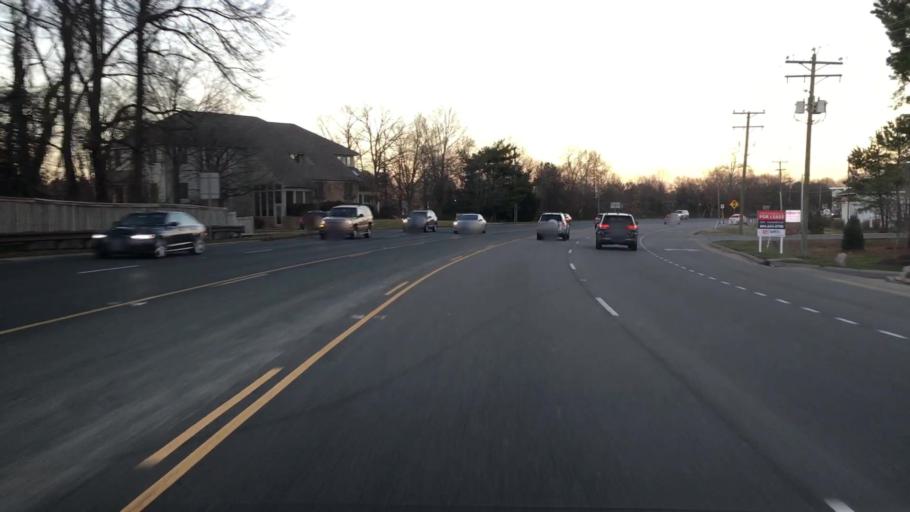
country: US
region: Virginia
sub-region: Chesterfield County
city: Bon Air
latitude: 37.5201
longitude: -77.6156
